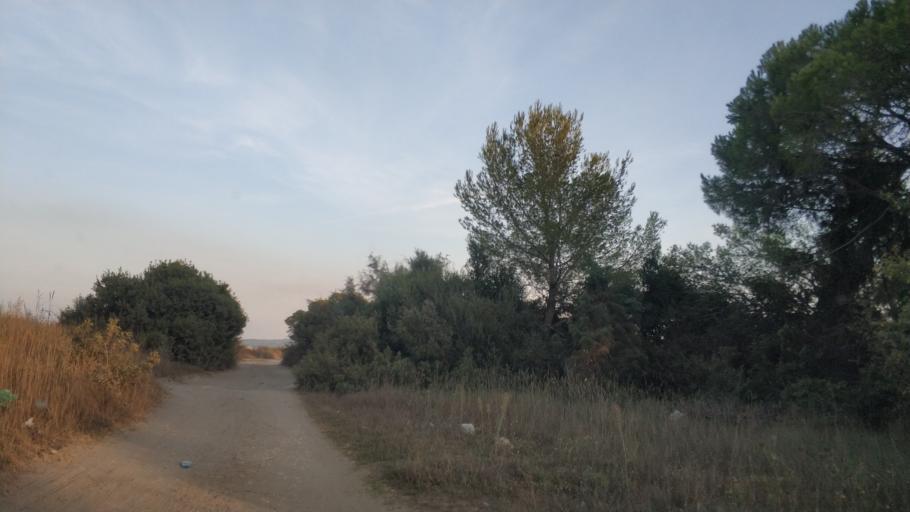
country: AL
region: Fier
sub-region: Rrethi i Lushnjes
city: Divjake
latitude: 40.9517
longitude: 19.4758
